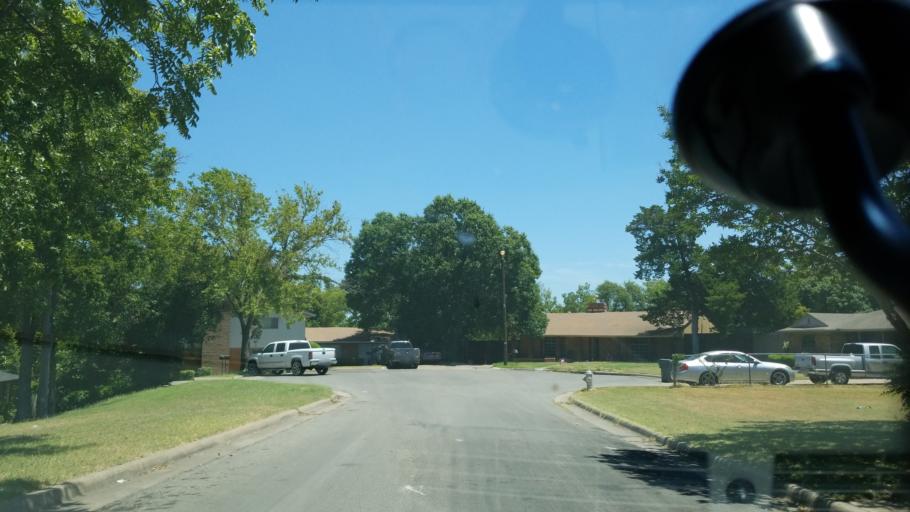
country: US
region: Texas
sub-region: Dallas County
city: Cockrell Hill
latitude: 32.6928
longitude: -96.8381
